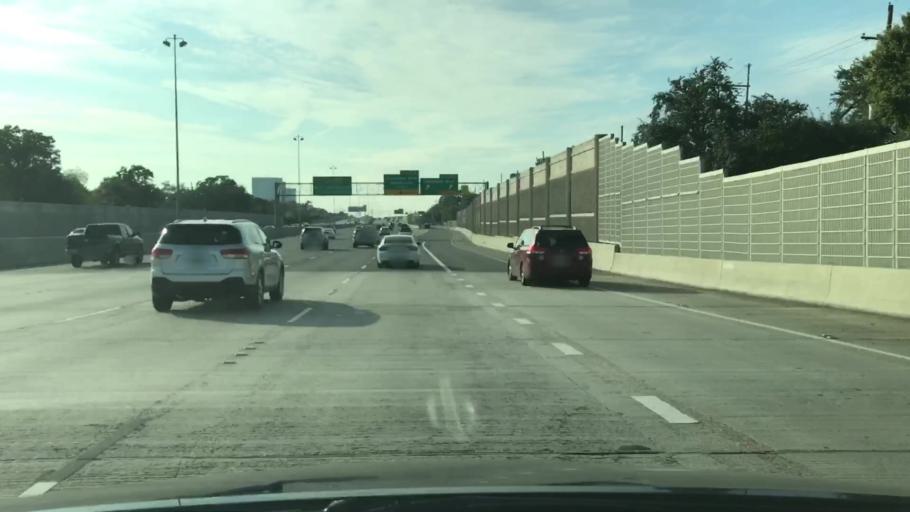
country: US
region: Louisiana
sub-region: Jefferson Parish
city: Metairie
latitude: 29.9970
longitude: -90.1347
